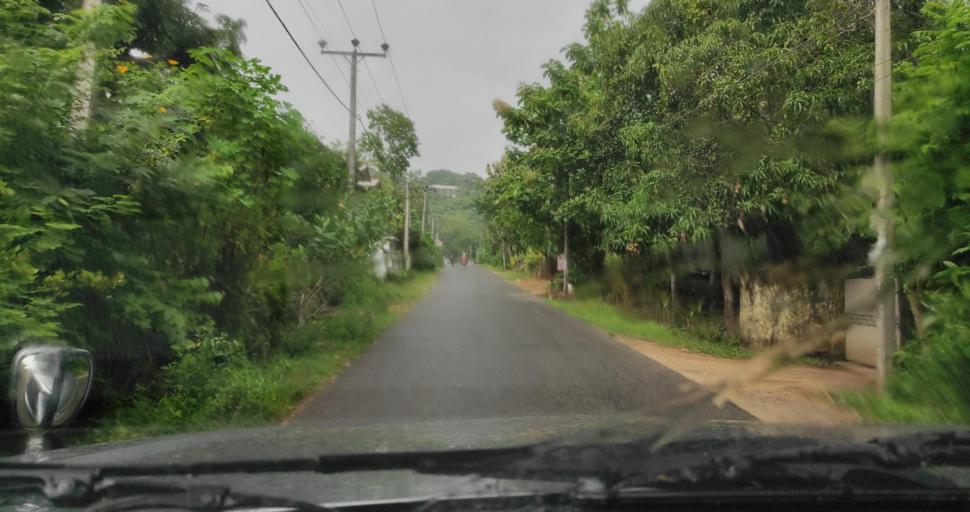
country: LK
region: Eastern Province
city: Trincomalee
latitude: 8.3675
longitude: 81.0068
